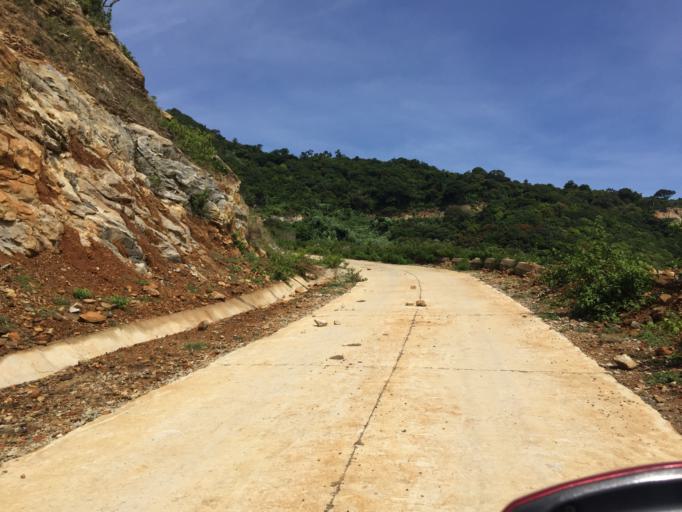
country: VN
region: Quang Nam
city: Hoi An
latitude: 15.9698
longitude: 108.5076
